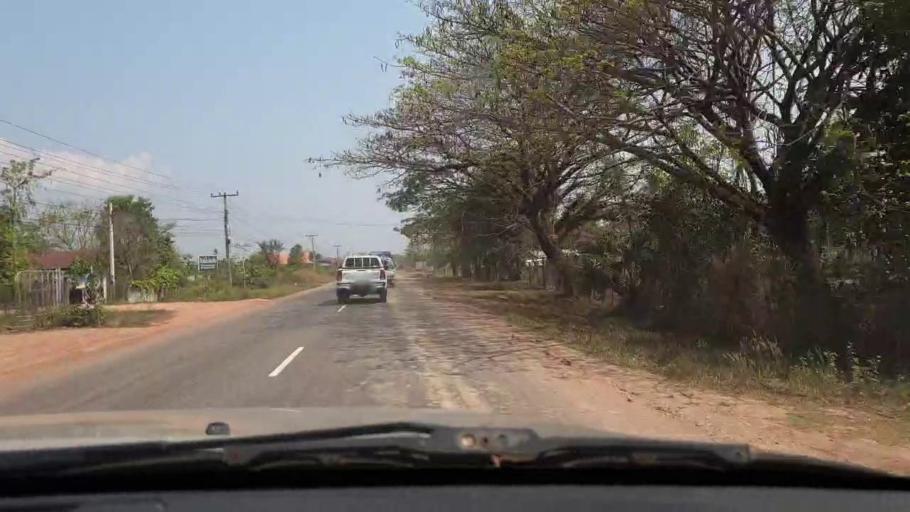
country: TH
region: Nong Khai
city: Phon Phisai
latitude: 18.1209
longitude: 103.0315
